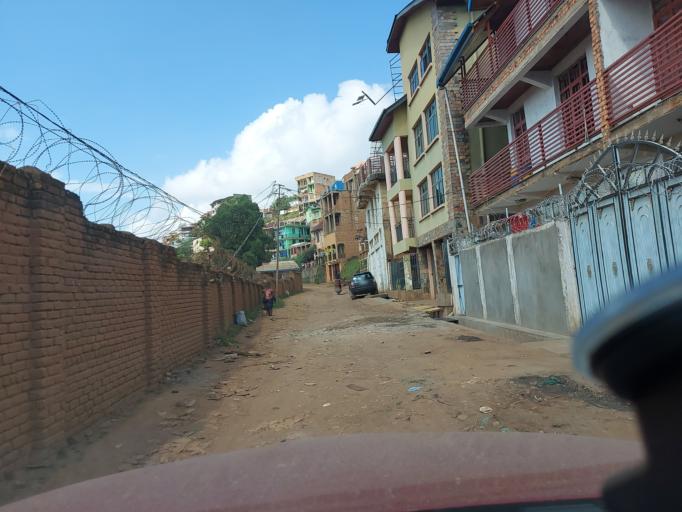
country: CD
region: South Kivu
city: Bukavu
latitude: -2.4982
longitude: 28.8617
